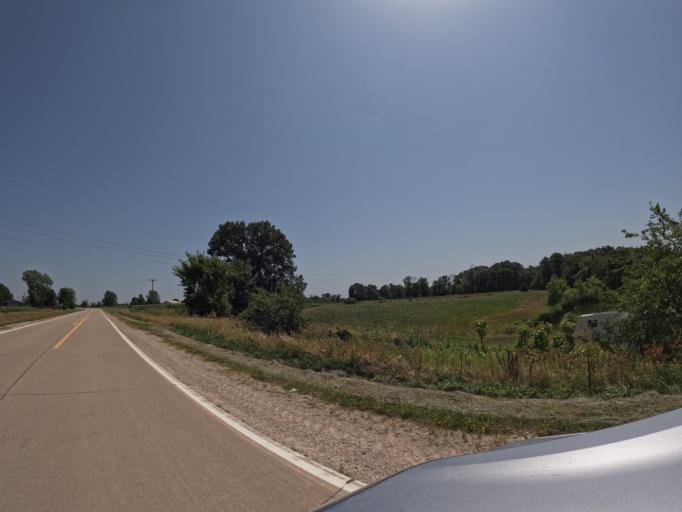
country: US
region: Iowa
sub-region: Henry County
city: Mount Pleasant
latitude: 40.9843
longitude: -91.6318
